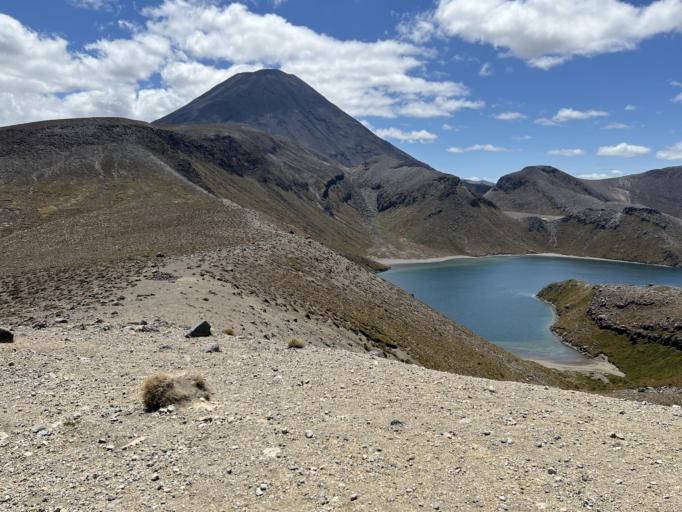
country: NZ
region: Waikato
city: Turangi
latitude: -39.1898
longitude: 175.6121
